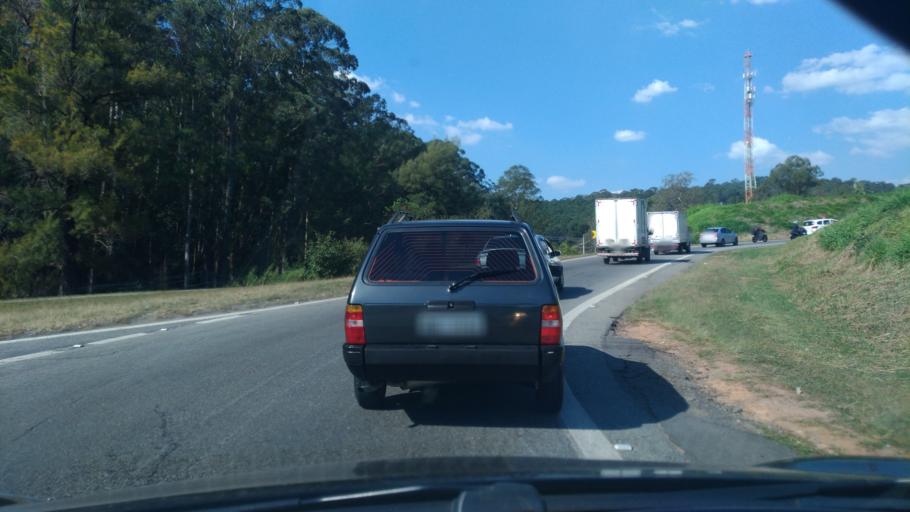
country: BR
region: Sao Paulo
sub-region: Caieiras
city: Caieiras
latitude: -23.4223
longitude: -46.7900
